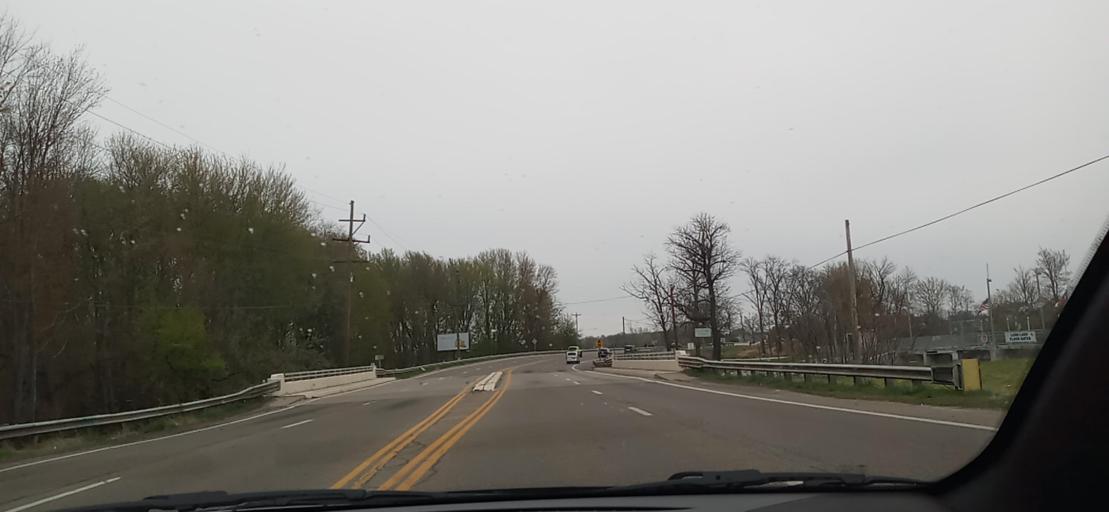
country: US
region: Ohio
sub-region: Summit County
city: Portage Lakes
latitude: 41.0211
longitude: -81.5501
